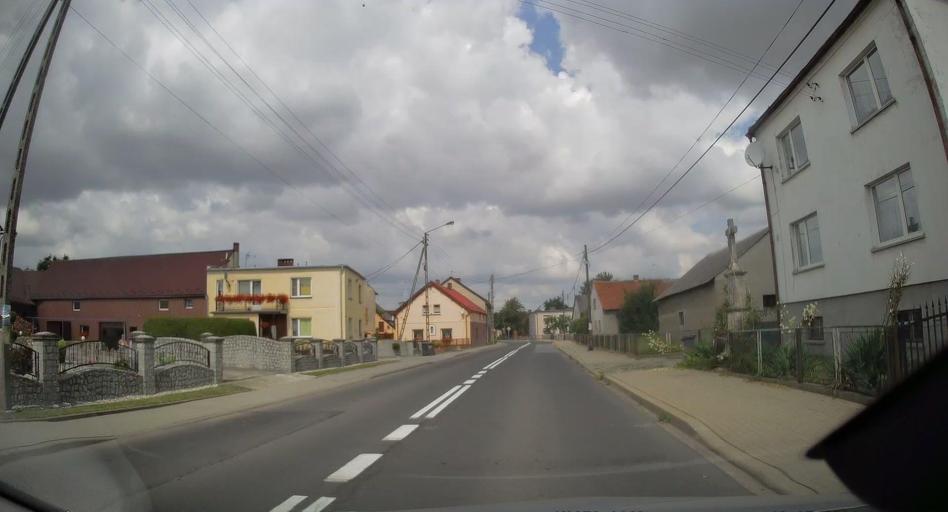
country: PL
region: Opole Voivodeship
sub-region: Powiat prudnicki
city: Twardawa
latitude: 50.3355
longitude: 17.9684
